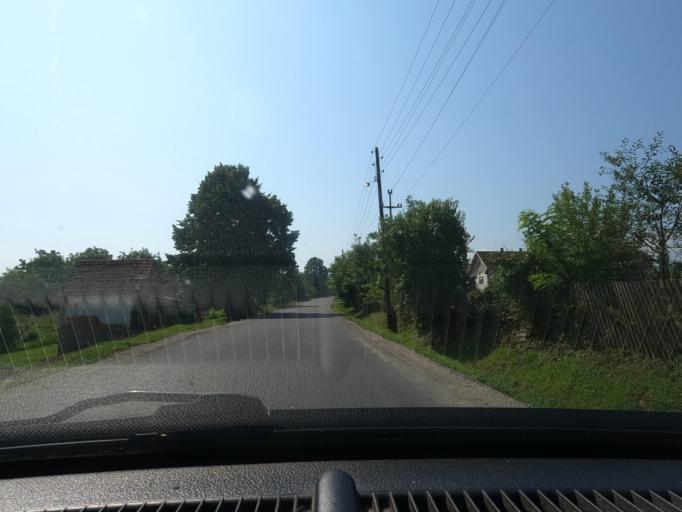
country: RS
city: Kozjak
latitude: 44.5665
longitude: 19.2878
